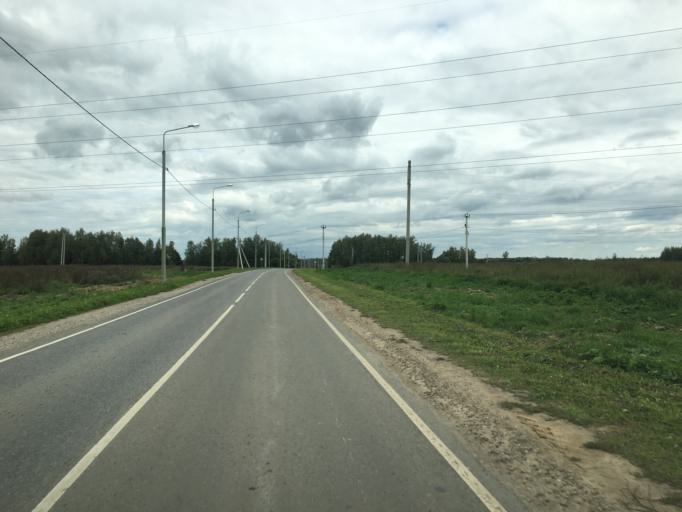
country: RU
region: Moskovskaya
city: Vatutinki
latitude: 55.4819
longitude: 37.4003
